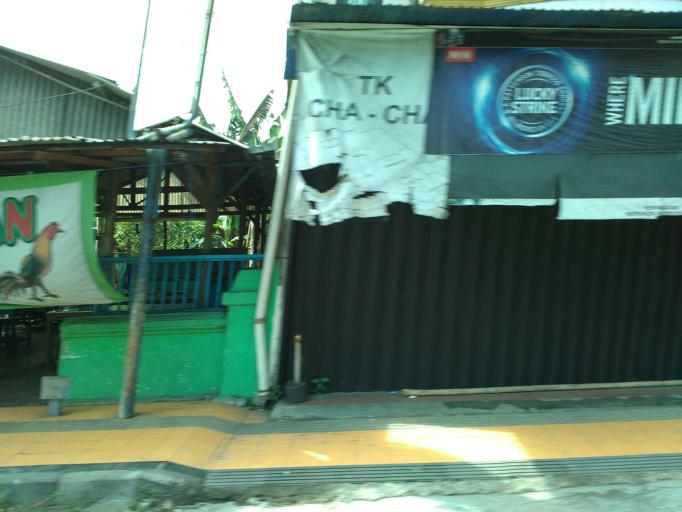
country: ID
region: Central Java
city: Candi Prambanan
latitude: -7.7553
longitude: 110.4958
